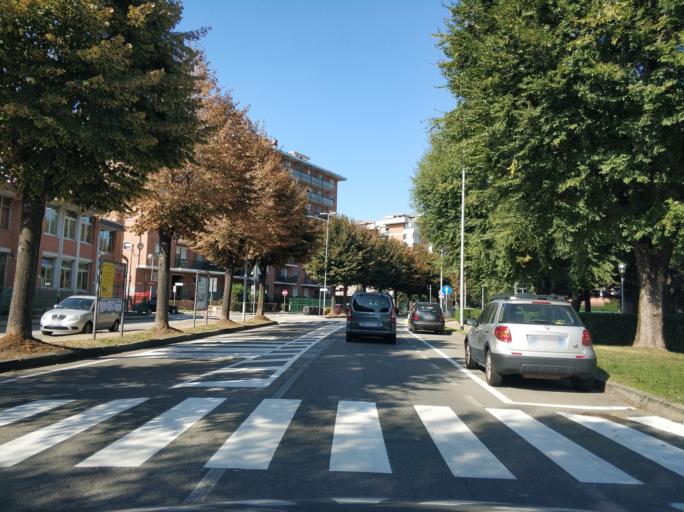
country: IT
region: Piedmont
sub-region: Provincia di Torino
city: Borgaro Torinese
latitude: 45.1542
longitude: 7.6581
